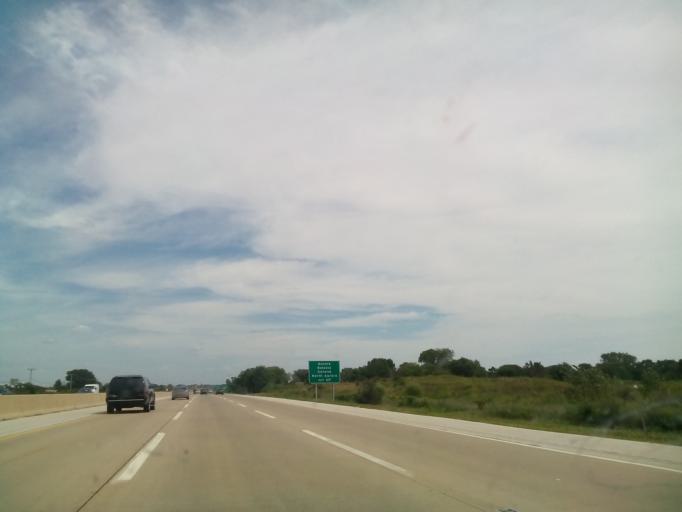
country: US
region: Illinois
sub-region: Kane County
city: North Aurora
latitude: 41.7952
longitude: -88.3488
